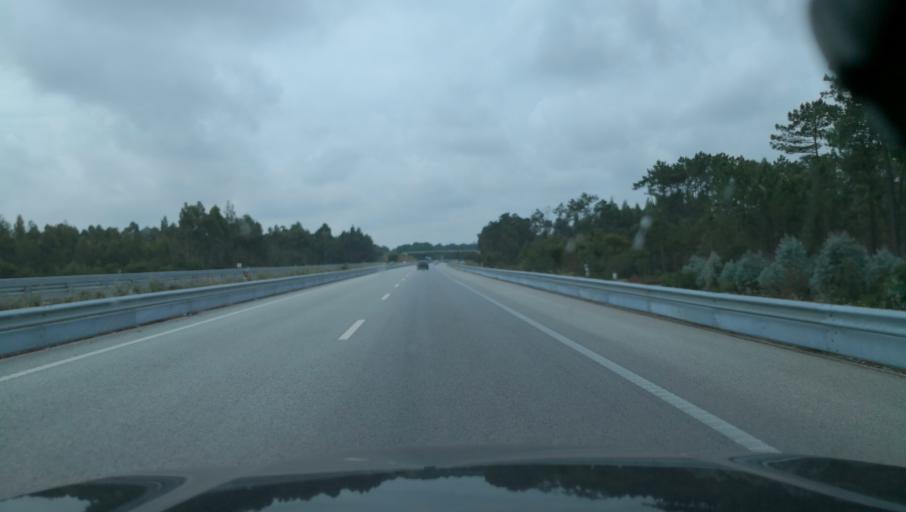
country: PT
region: Coimbra
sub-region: Figueira da Foz
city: Alhadas
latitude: 40.2399
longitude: -8.7843
